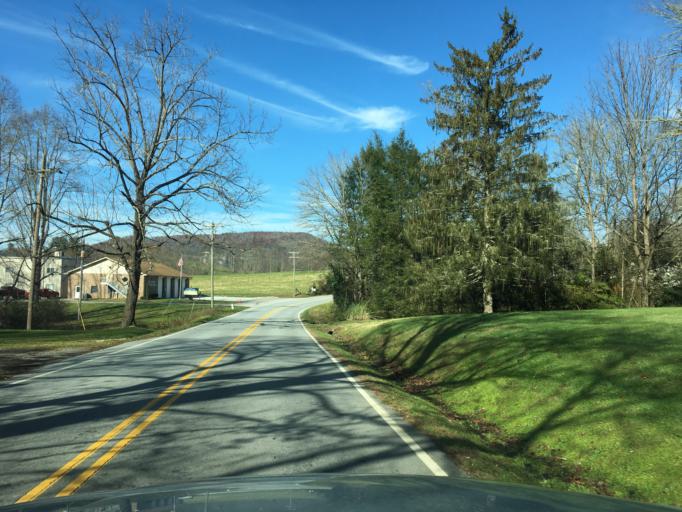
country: US
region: North Carolina
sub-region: Henderson County
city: Etowah
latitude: 35.2561
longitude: -82.6342
